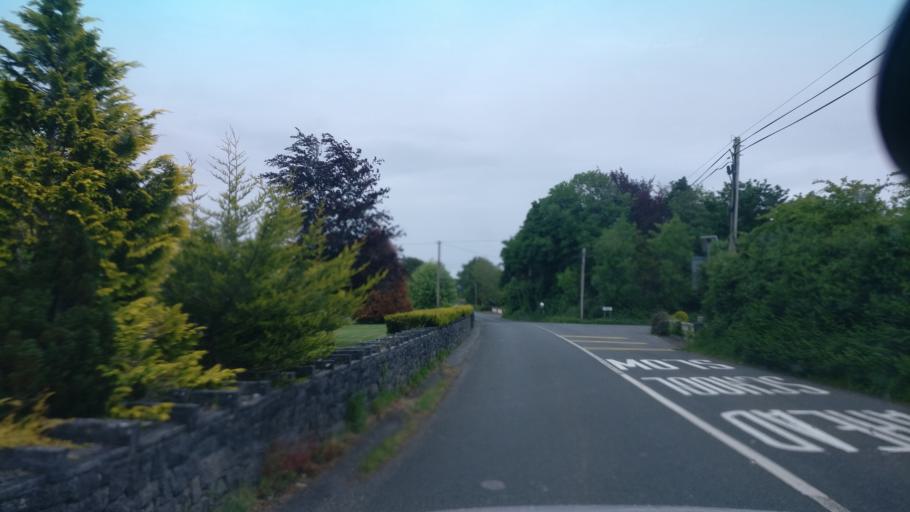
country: IE
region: Connaught
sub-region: County Galway
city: Gort
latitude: 53.0678
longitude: -8.7808
